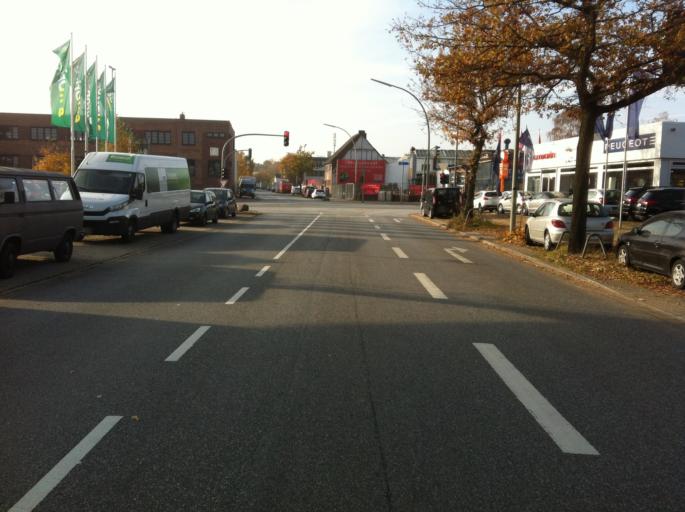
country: DE
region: Hamburg
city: Altona
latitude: 53.5683
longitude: 9.9360
